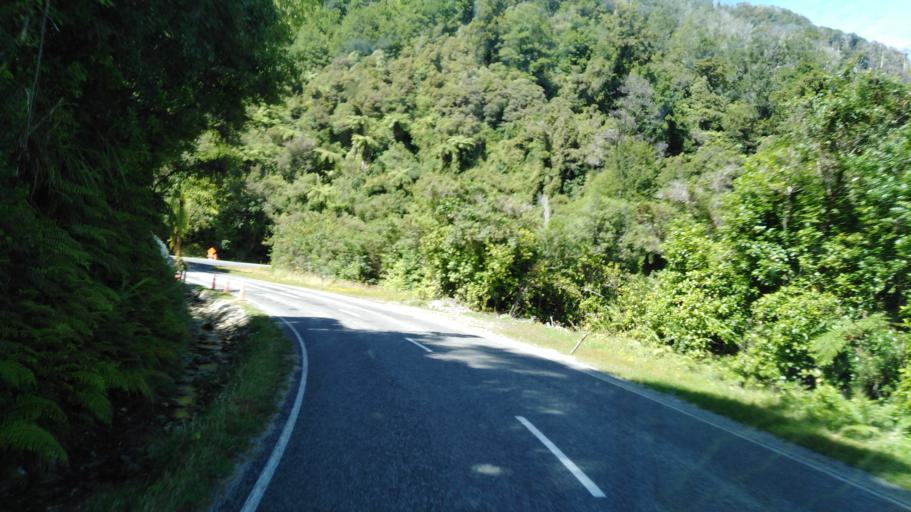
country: NZ
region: West Coast
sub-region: Buller District
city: Westport
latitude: -41.4926
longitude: 172.0495
